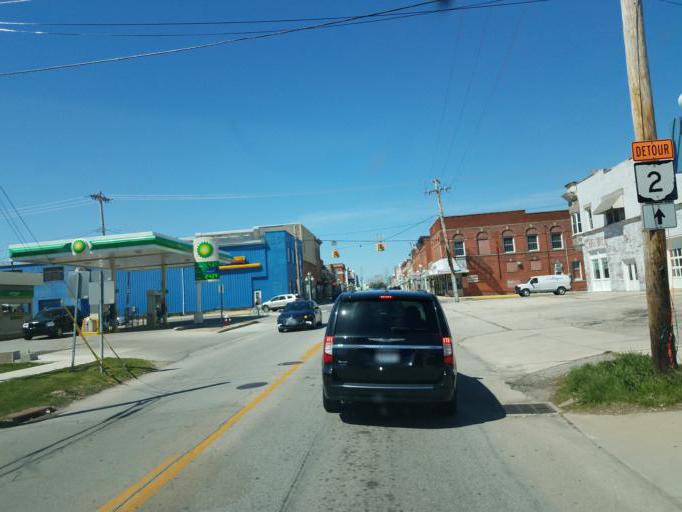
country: US
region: Ohio
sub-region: Ottawa County
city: Oak Harbor
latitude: 41.5076
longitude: -83.1443
